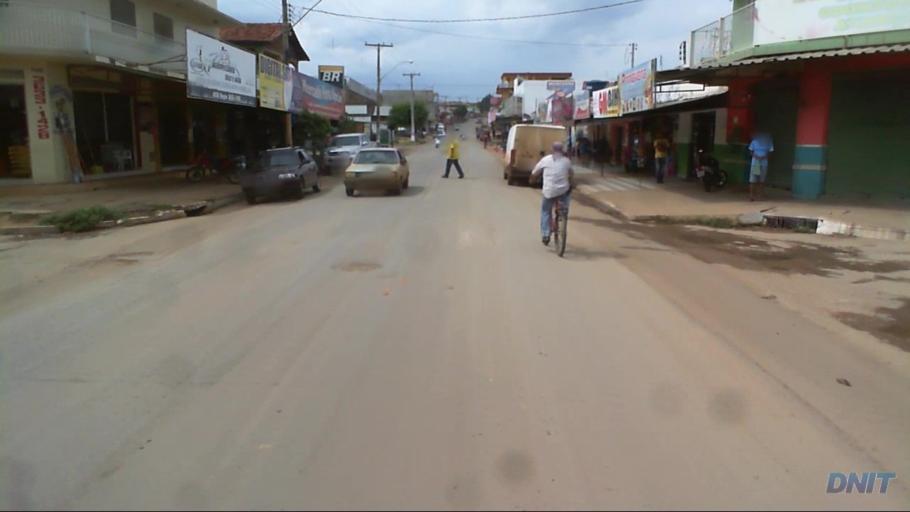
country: BR
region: Goias
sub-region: Padre Bernardo
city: Padre Bernardo
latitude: -15.1690
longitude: -48.2848
